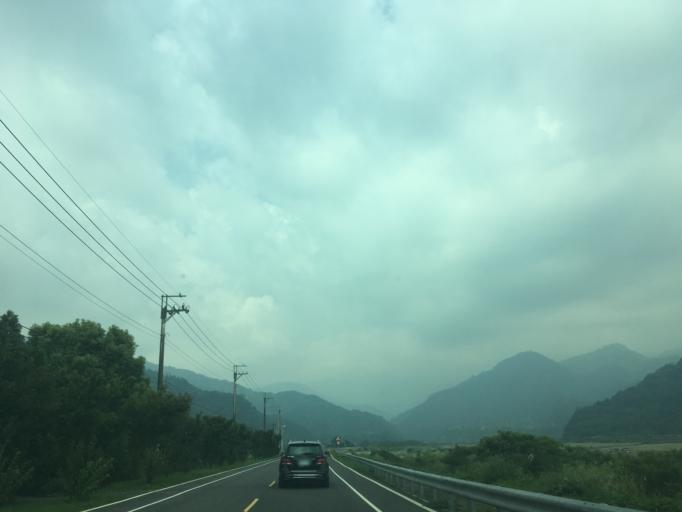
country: TW
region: Taiwan
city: Fengyuan
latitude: 24.2959
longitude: 120.8770
